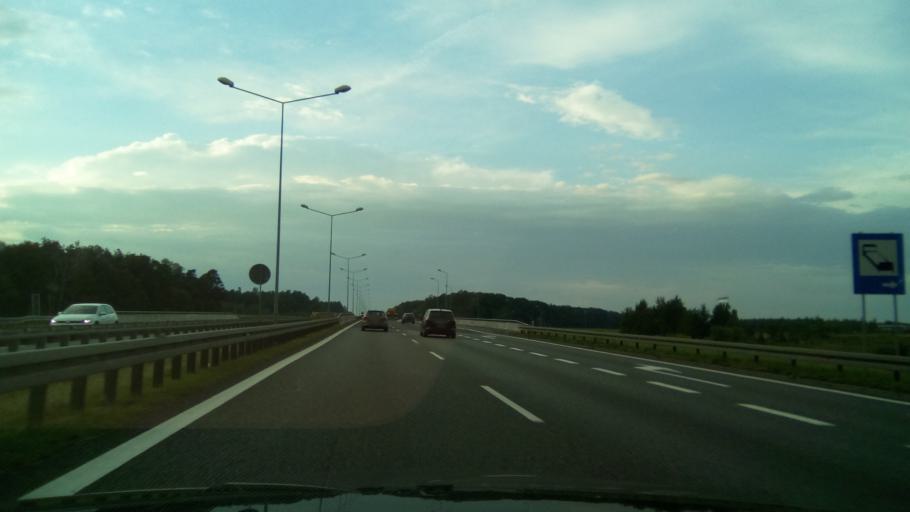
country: PL
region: Silesian Voivodeship
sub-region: Powiat gliwicki
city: Sosnicowice
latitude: 50.2776
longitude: 18.5734
